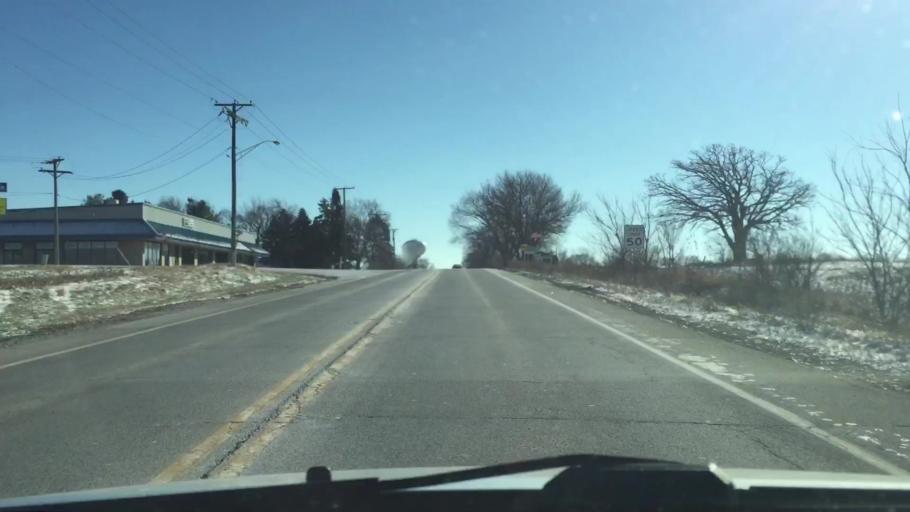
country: US
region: Illinois
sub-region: McHenry County
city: McCullom Lake
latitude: 42.3848
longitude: -88.2776
